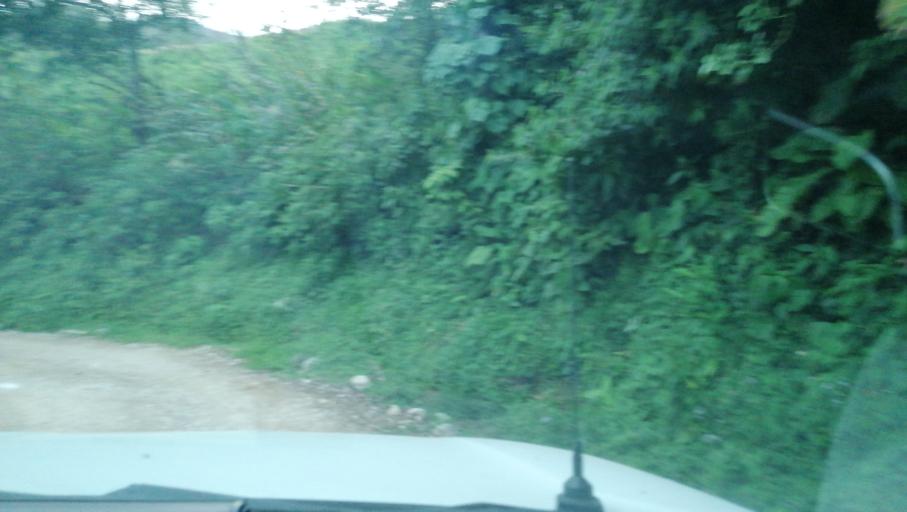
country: MX
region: Chiapas
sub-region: Francisco Leon
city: San Miguel la Sardina
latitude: 17.2928
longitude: -93.2691
